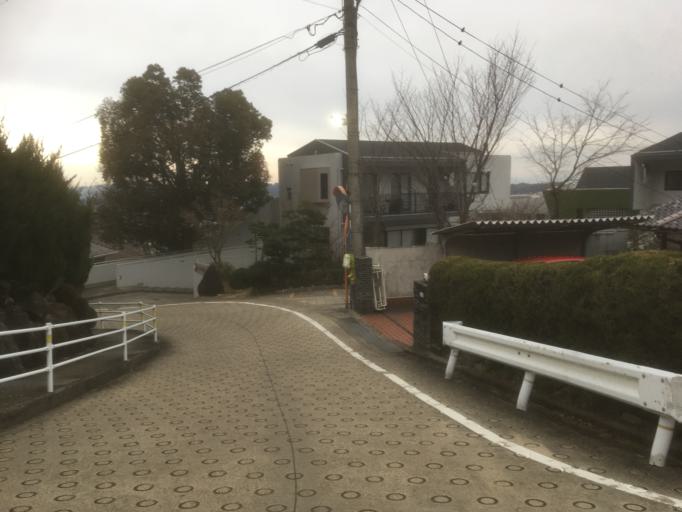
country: JP
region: Nara
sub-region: Ikoma-shi
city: Ikoma
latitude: 34.6865
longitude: 135.6935
